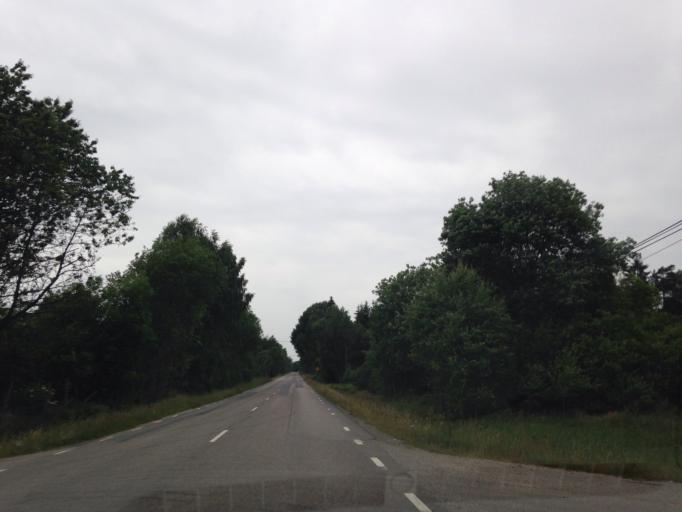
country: SE
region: Vaestra Goetaland
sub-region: Harryda Kommun
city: Hindas
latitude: 57.6729
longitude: 12.3505
